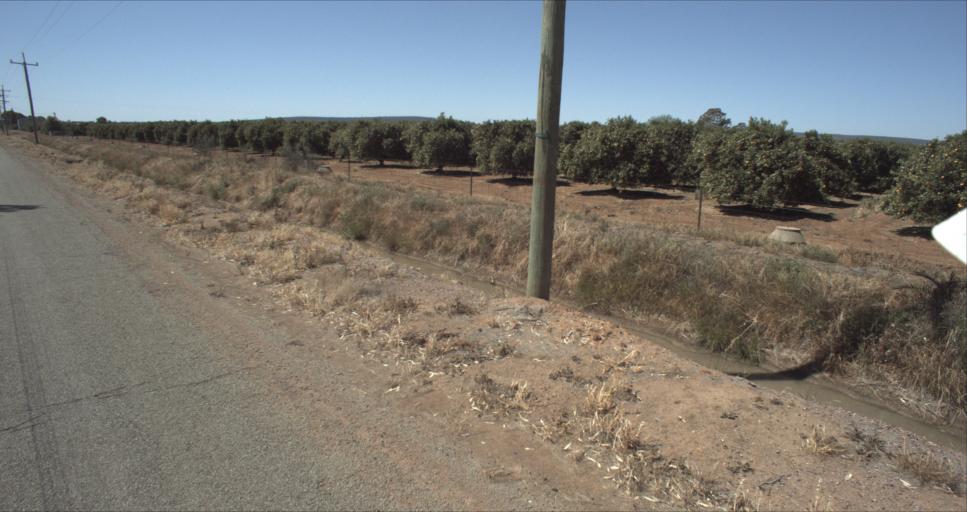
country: AU
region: New South Wales
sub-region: Leeton
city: Leeton
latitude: -34.4989
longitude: 146.4207
